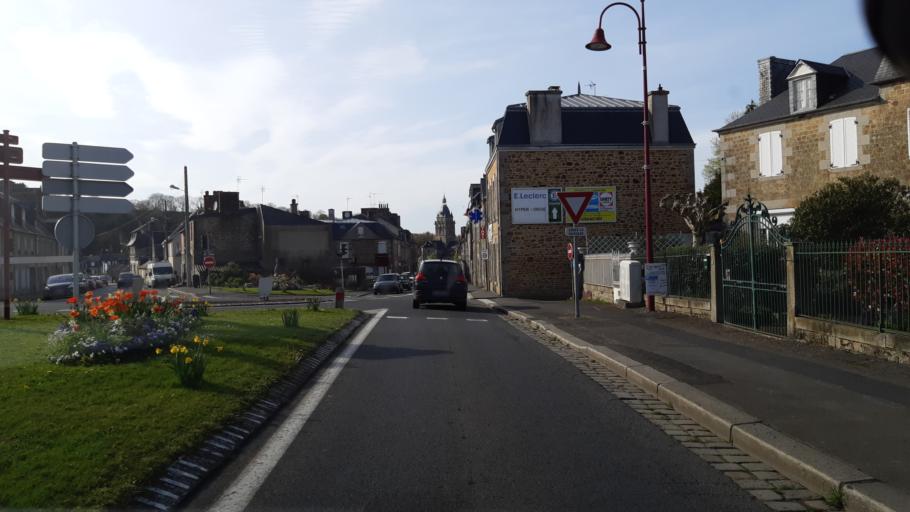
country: FR
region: Lower Normandy
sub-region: Departement de la Manche
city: Villedieu-les-Poeles
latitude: 48.8351
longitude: -1.2188
